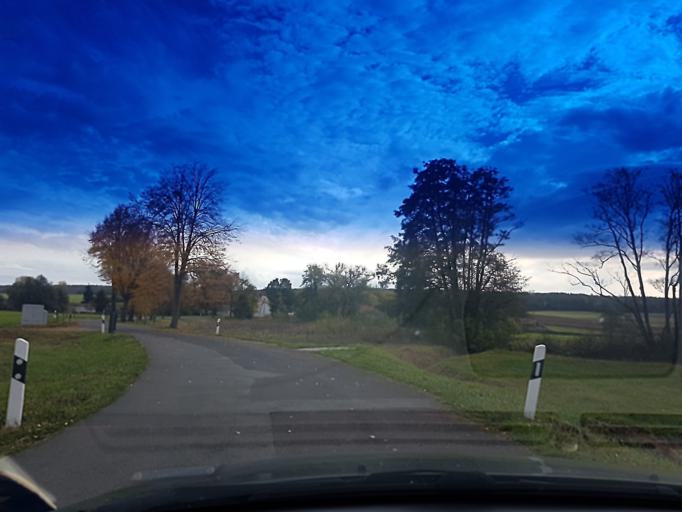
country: DE
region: Bavaria
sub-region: Regierungsbezirk Mittelfranken
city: Wachenroth
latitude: 49.7475
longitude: 10.6888
